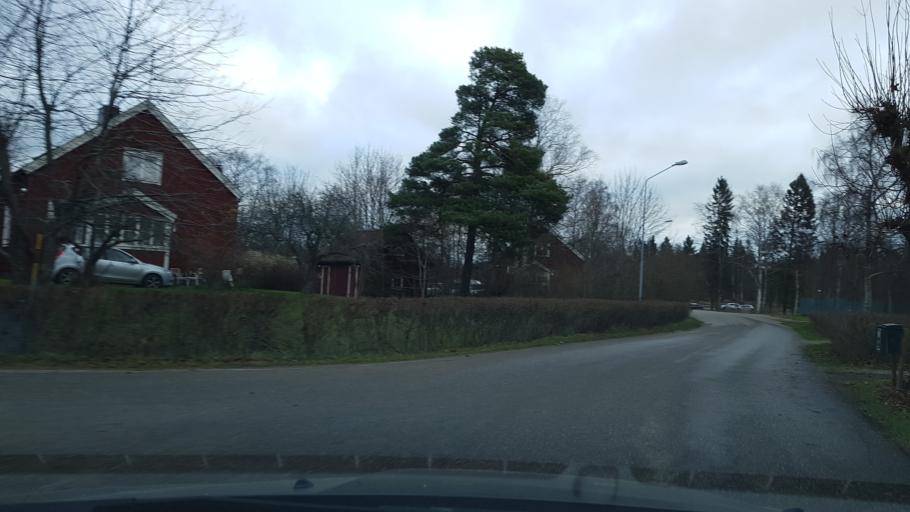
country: SE
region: Stockholm
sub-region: Norrtalje Kommun
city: Hallstavik
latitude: 60.0616
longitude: 18.5975
